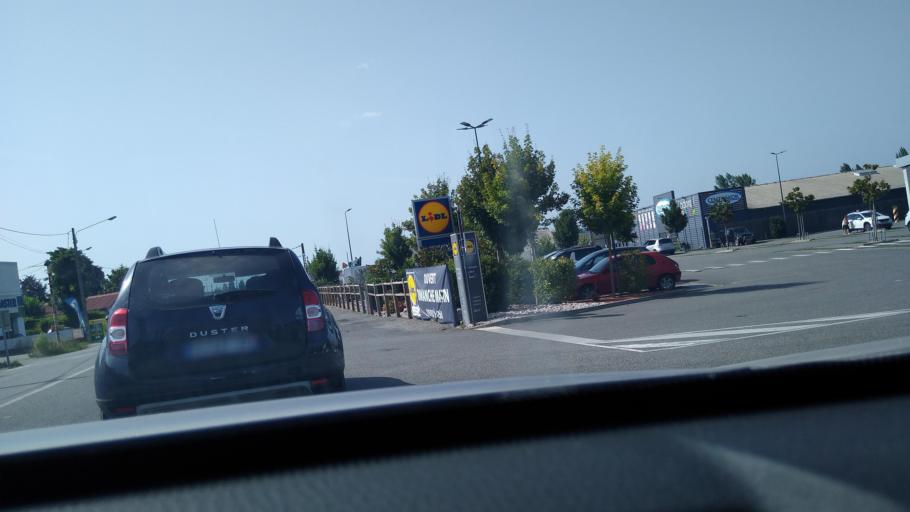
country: FR
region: Midi-Pyrenees
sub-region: Departement de l'Ariege
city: Saint-Lizier
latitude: 43.0040
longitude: 1.1289
